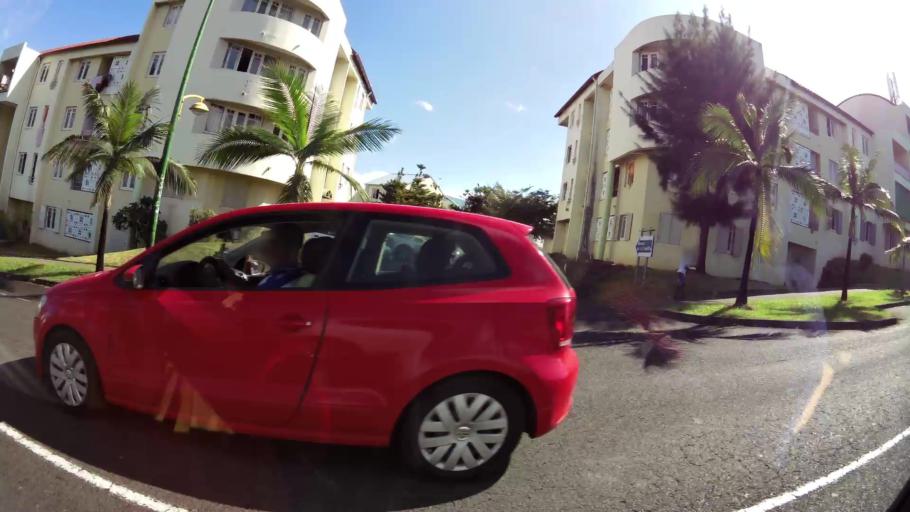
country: RE
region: Reunion
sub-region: Reunion
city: Le Tampon
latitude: -21.2754
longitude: 55.5054
